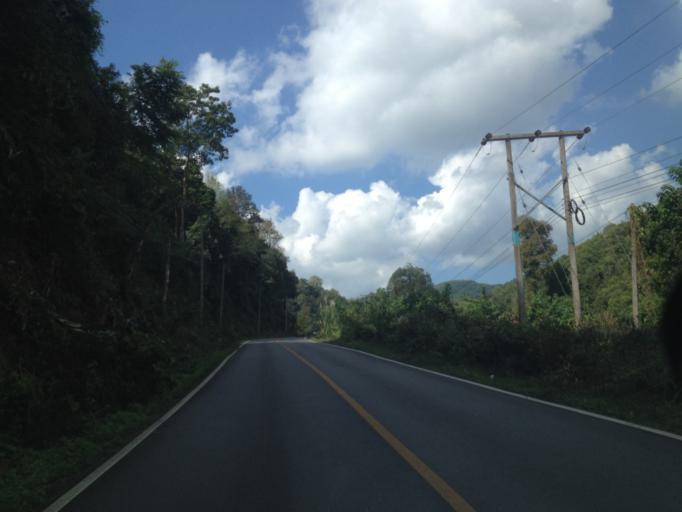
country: TH
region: Mae Hong Son
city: Ban Huai I Huak
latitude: 18.1477
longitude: 98.1489
